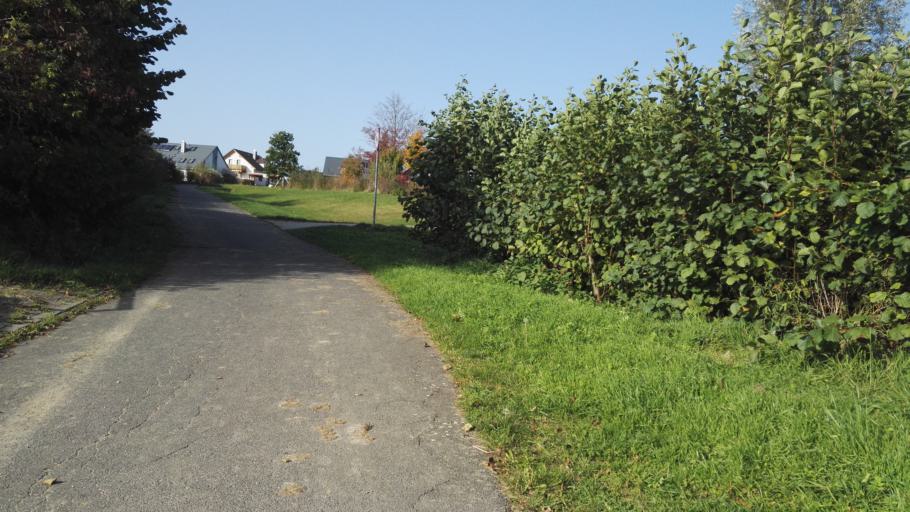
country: DE
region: Lower Saxony
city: Hildesheim
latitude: 52.1246
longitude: 9.9927
